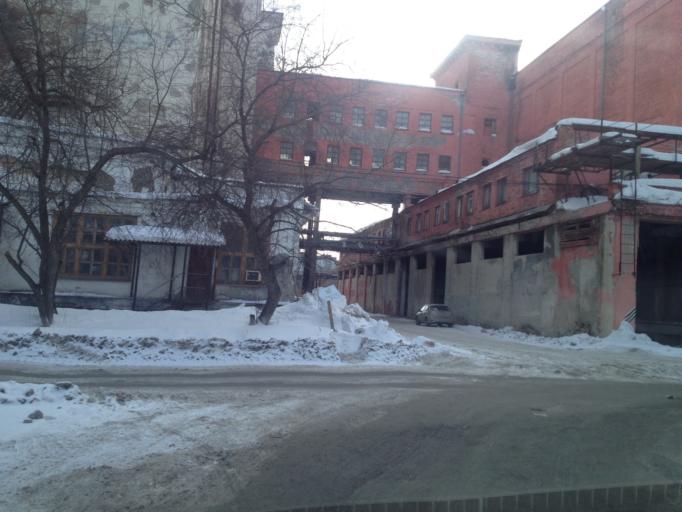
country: RU
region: Sverdlovsk
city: Sovkhoznyy
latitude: 56.7786
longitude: 60.6163
